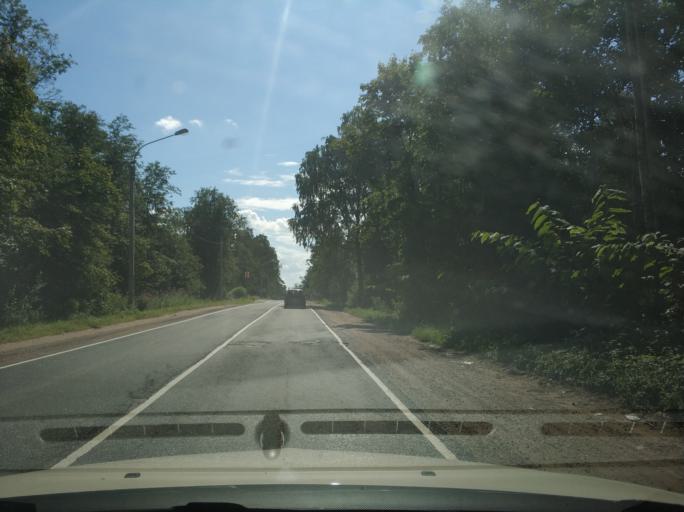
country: RU
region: Leningrad
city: Osel'ki
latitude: 60.2152
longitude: 30.5586
